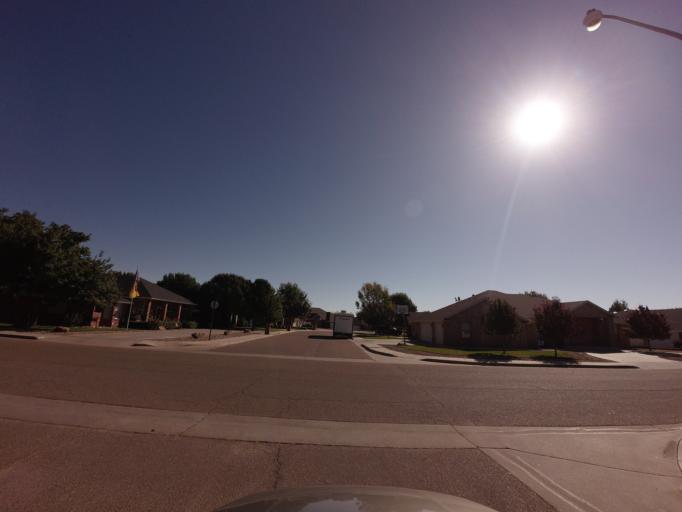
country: US
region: New Mexico
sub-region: Curry County
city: Clovis
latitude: 34.4262
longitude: -103.1723
